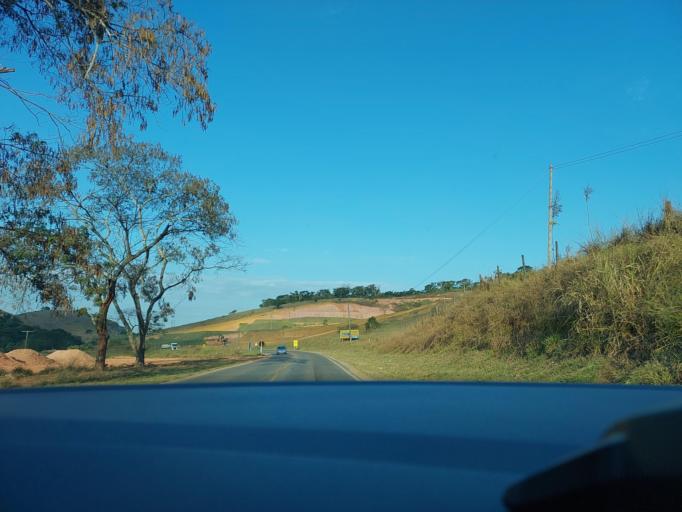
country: BR
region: Minas Gerais
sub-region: Muriae
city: Muriae
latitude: -21.1128
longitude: -42.4425
